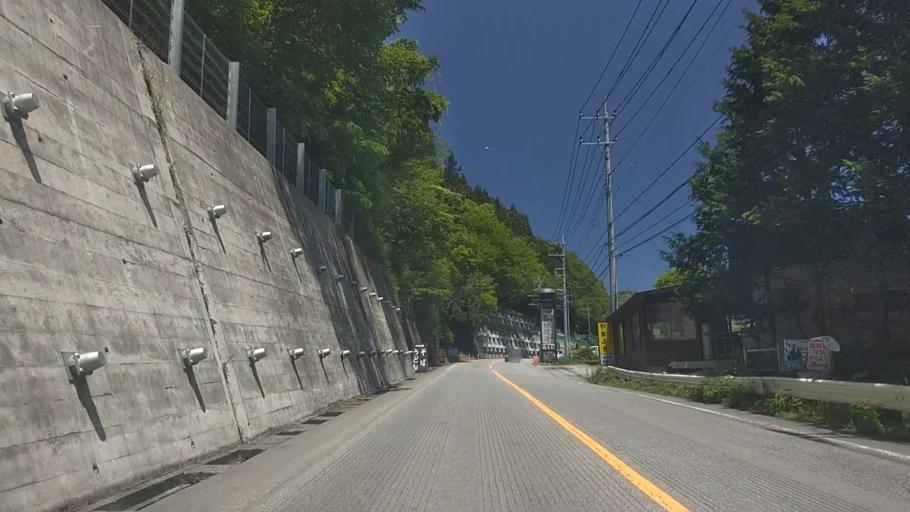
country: JP
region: Yamanashi
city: Nirasaki
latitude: 35.8810
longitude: 138.4266
